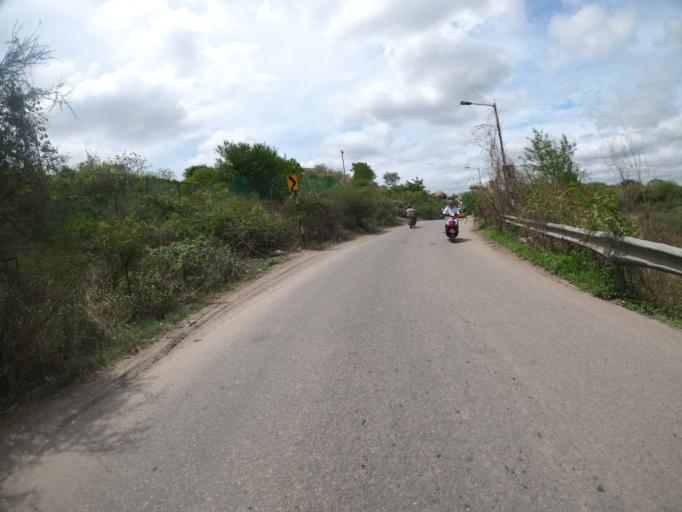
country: IN
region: Telangana
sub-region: Hyderabad
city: Hyderabad
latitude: 17.3166
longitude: 78.3719
